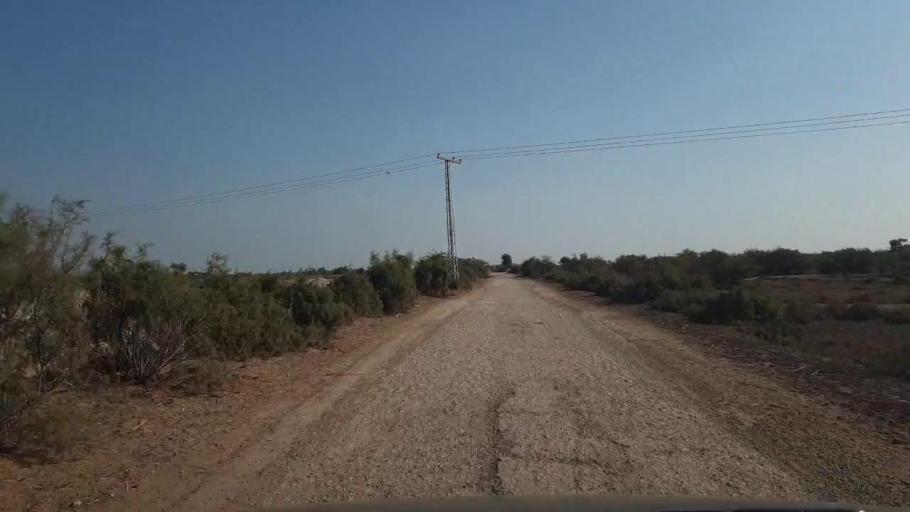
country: PK
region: Sindh
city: Shahpur Chakar
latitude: 26.1516
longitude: 68.6770
